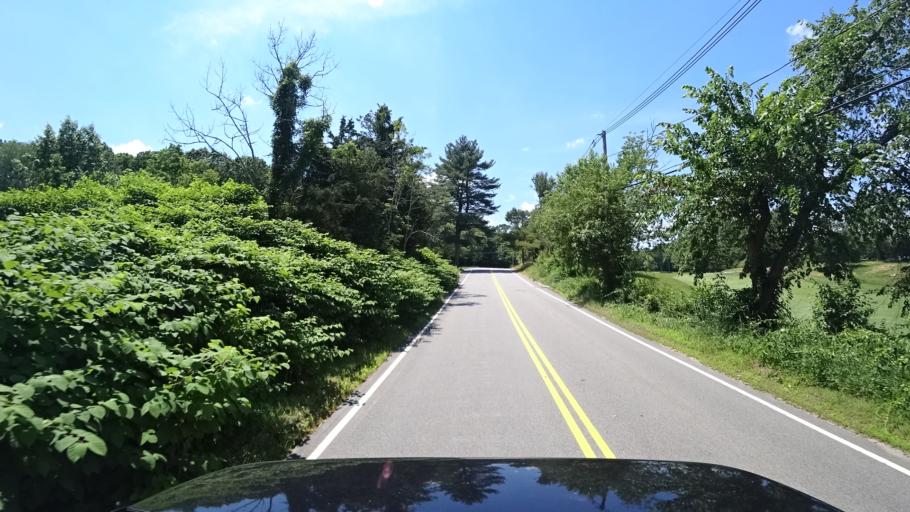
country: US
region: Massachusetts
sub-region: Norfolk County
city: Needham
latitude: 42.2537
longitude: -71.2249
